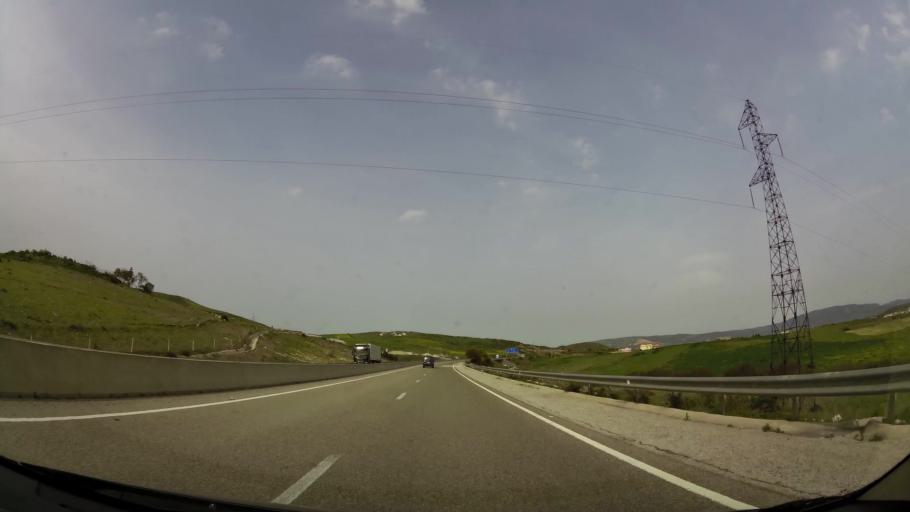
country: MA
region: Tanger-Tetouan
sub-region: Tanger-Assilah
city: Tangier
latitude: 35.6825
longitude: -5.7220
